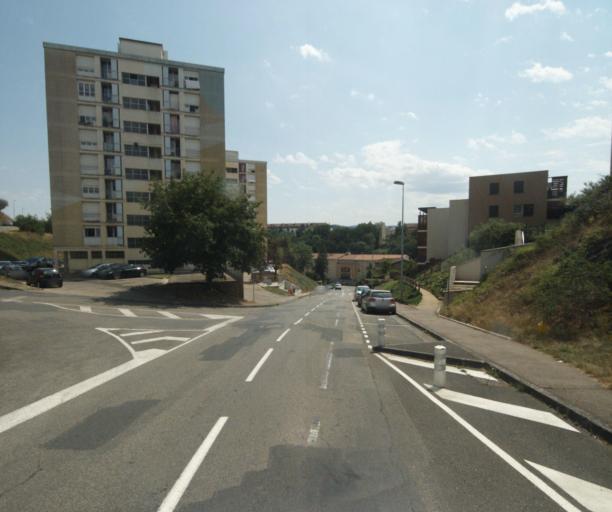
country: FR
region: Rhone-Alpes
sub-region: Departement du Rhone
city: Saint-Germain-Nuelles
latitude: 45.8391
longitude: 4.6108
